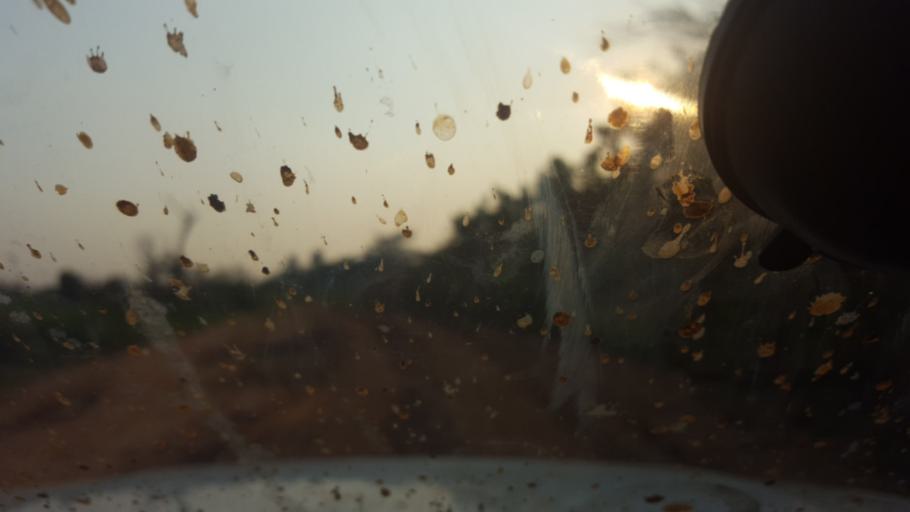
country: CD
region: Bandundu
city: Mushie
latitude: -3.7536
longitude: 16.6709
